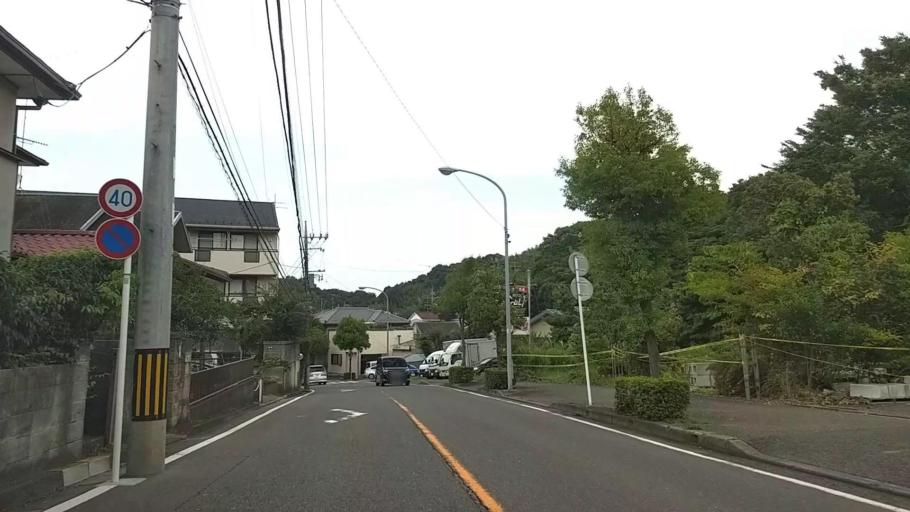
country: JP
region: Kanagawa
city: Yokohama
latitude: 35.4982
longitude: 139.5657
